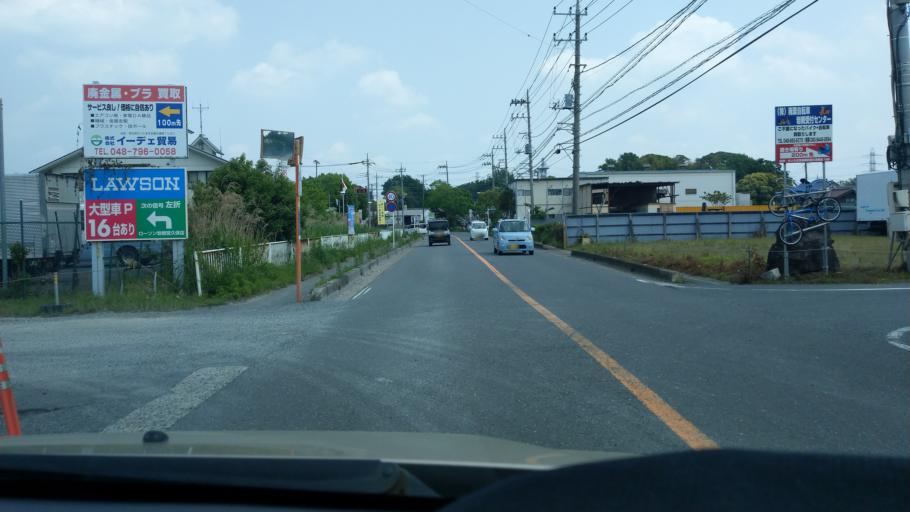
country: JP
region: Saitama
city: Iwatsuki
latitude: 35.9149
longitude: 139.7151
